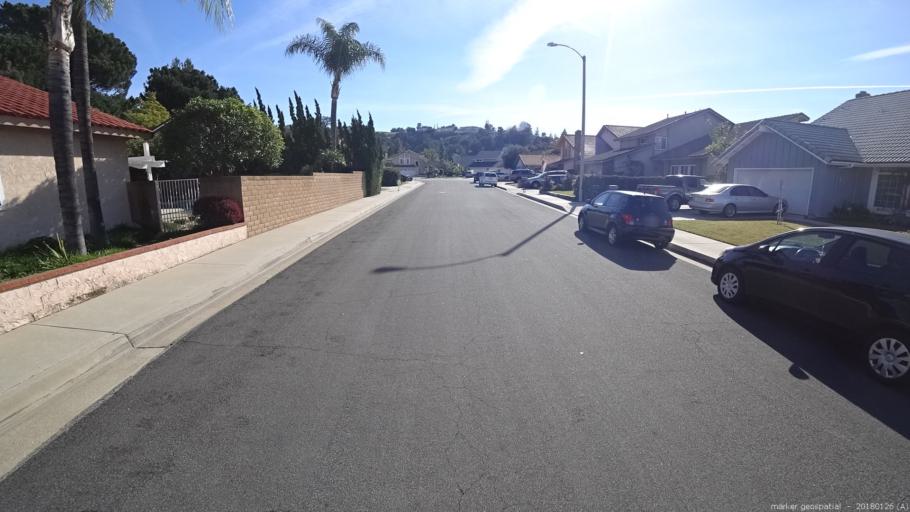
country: US
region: California
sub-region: Los Angeles County
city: Diamond Bar
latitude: 33.9951
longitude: -117.8077
